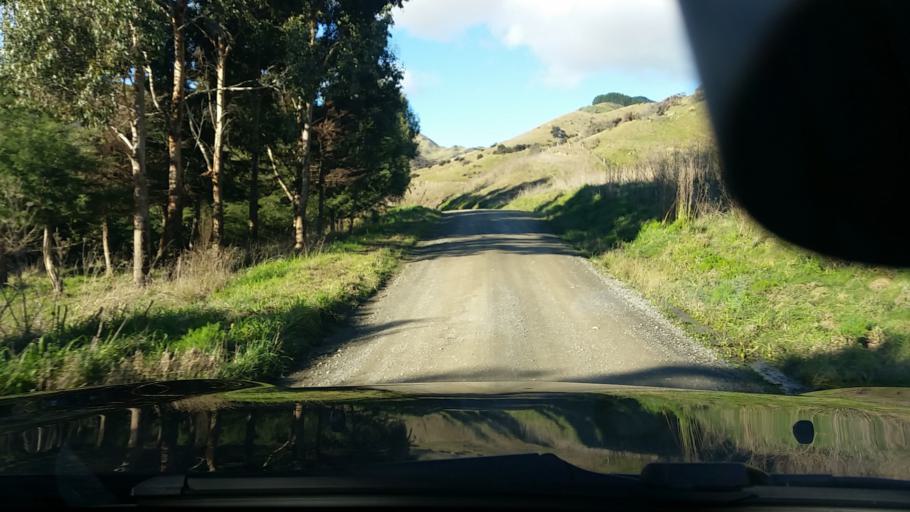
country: NZ
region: Marlborough
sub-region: Marlborough District
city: Blenheim
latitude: -41.6045
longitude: 173.9654
